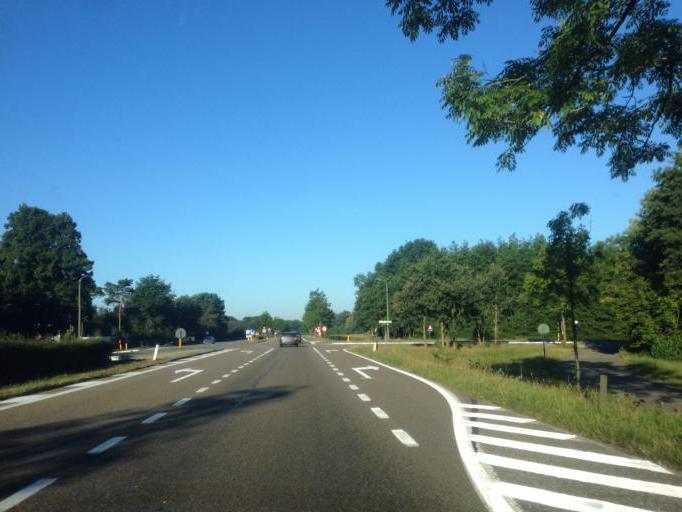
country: BE
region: Flanders
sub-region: Provincie Antwerpen
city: Mol
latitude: 51.1712
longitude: 5.0902
